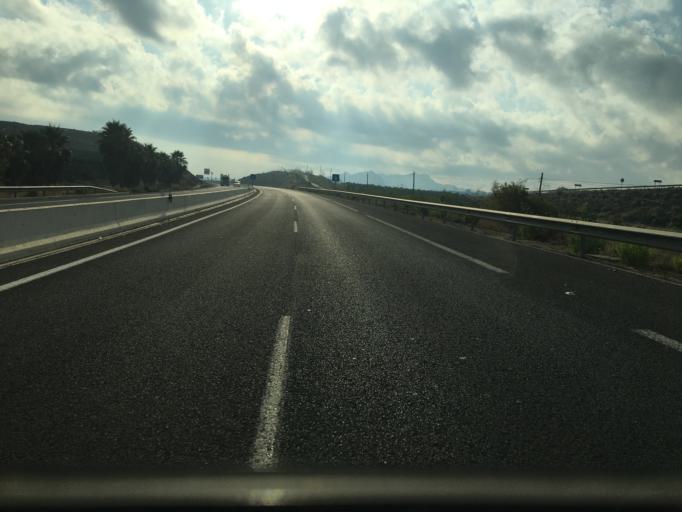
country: ES
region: Murcia
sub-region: Murcia
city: Beniel
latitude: 37.9950
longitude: -0.9963
